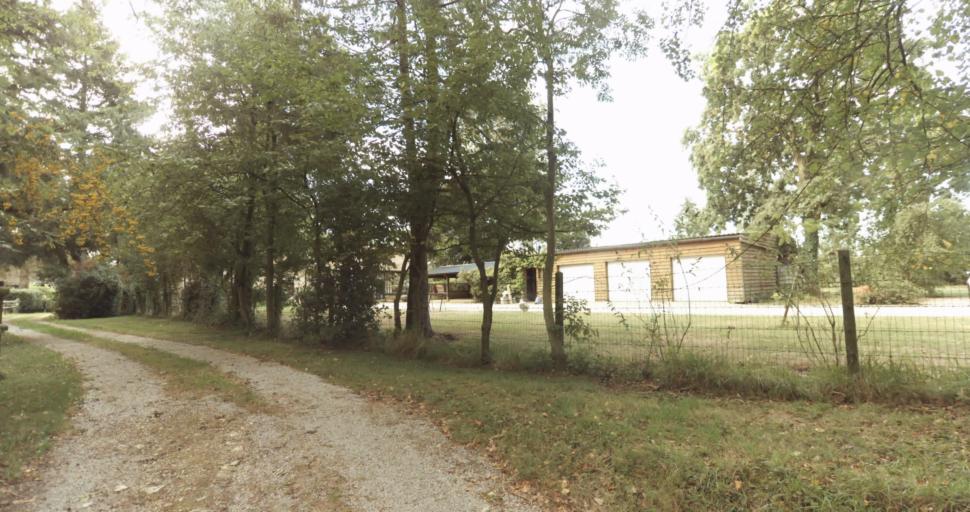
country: FR
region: Lower Normandy
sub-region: Departement de l'Orne
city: Vimoutiers
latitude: 48.8883
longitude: 0.2400
